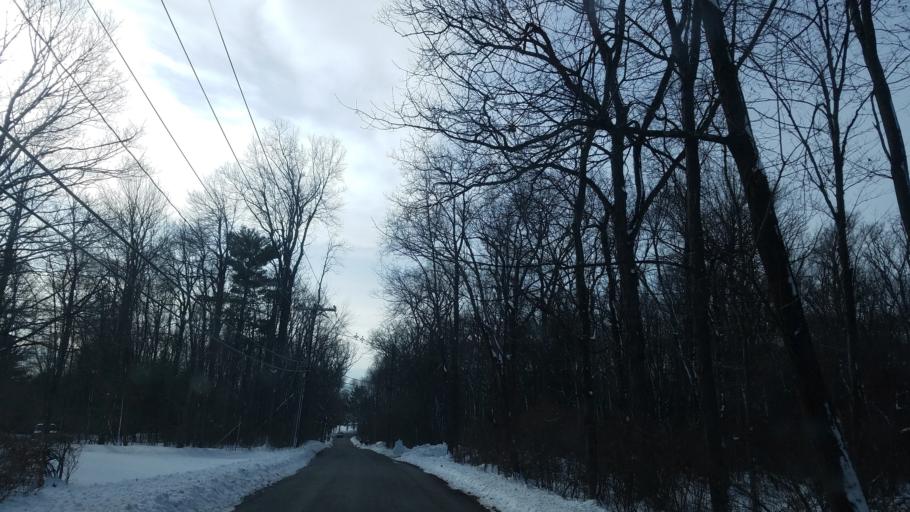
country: US
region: Connecticut
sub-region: Hartford County
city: Canton Valley
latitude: 41.8455
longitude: -72.9071
